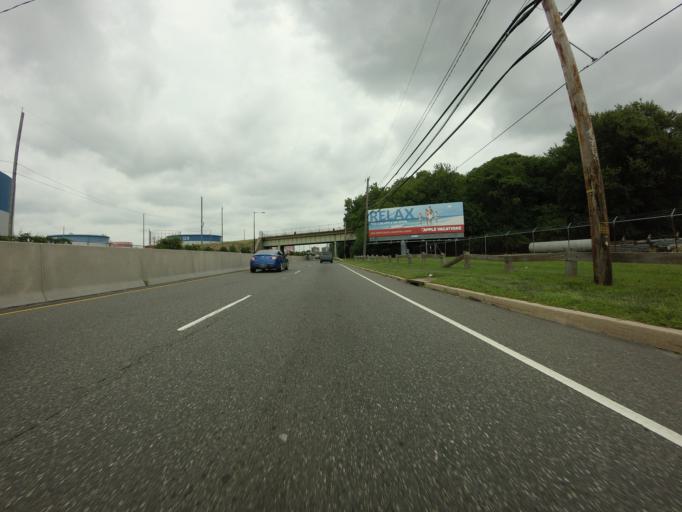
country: US
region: Pennsylvania
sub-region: Philadelphia County
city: Philadelphia
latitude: 39.9152
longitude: -75.1918
